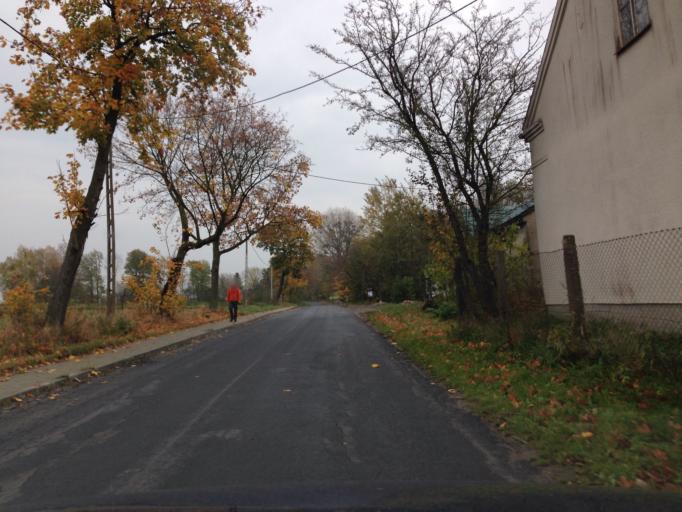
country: PL
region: Kujawsko-Pomorskie
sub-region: Powiat rypinski
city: Rypin
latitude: 53.1225
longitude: 19.4242
